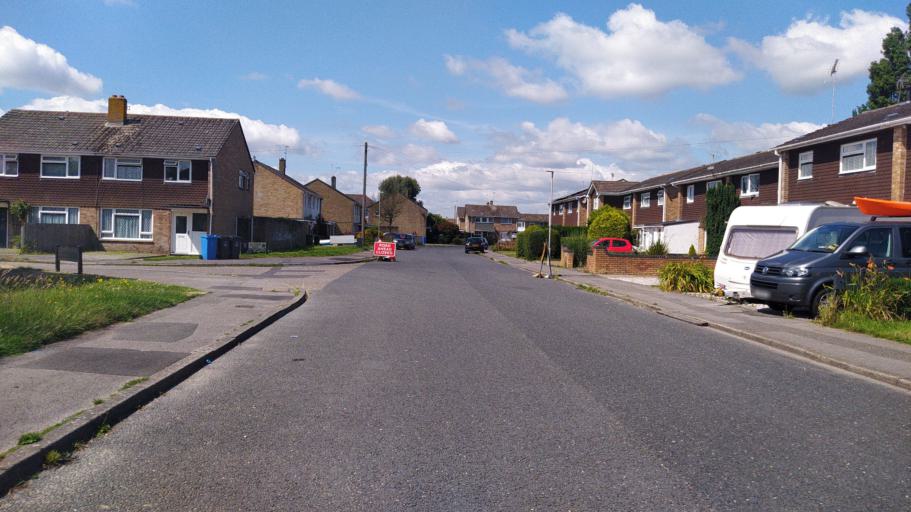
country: GB
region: England
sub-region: Poole
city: Poole
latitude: 50.7246
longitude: -2.0306
